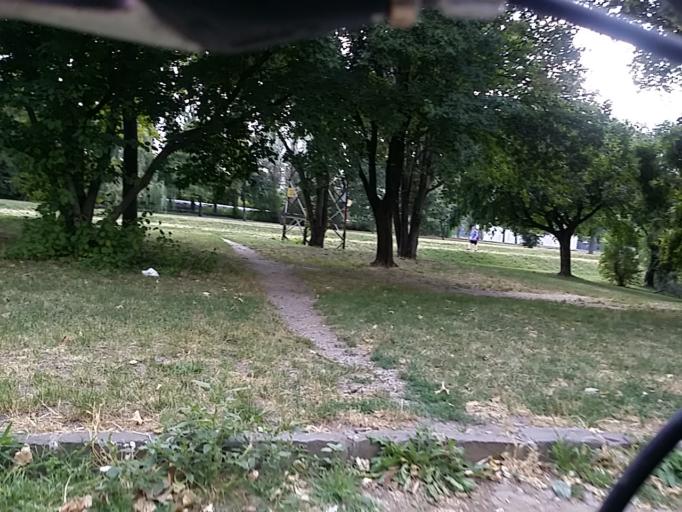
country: HU
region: Budapest
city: Budapest XIII. keruelet
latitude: 47.5402
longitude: 19.0823
